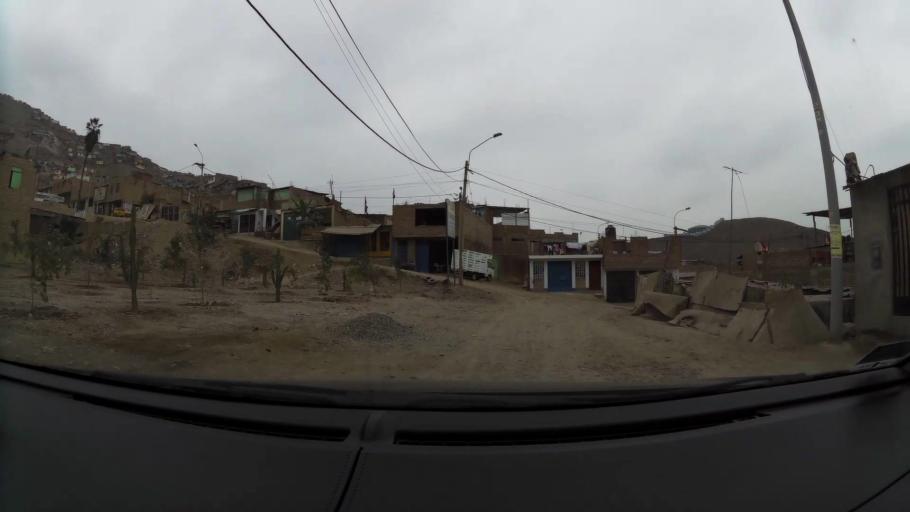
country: PE
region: Lima
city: Ventanilla
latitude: -11.9332
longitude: -77.0902
